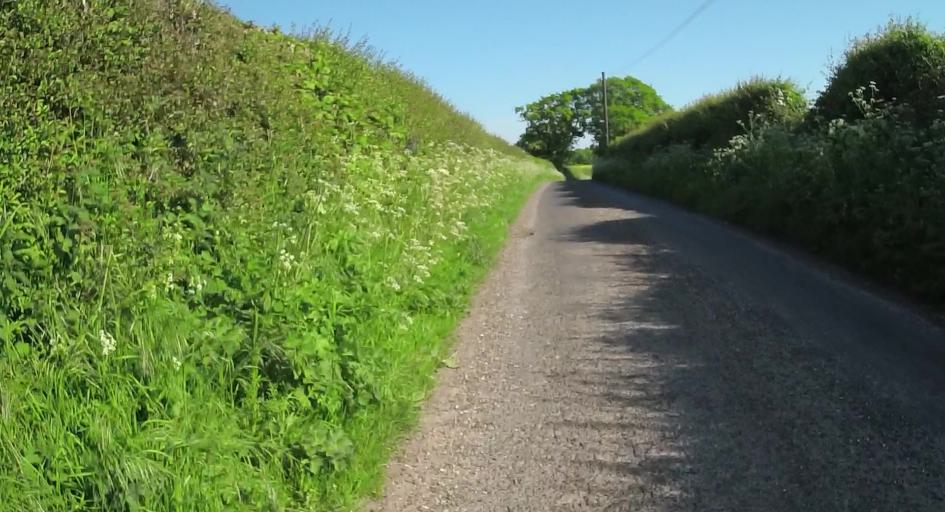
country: GB
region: England
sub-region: Hampshire
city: Overton
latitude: 51.1587
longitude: -1.1805
